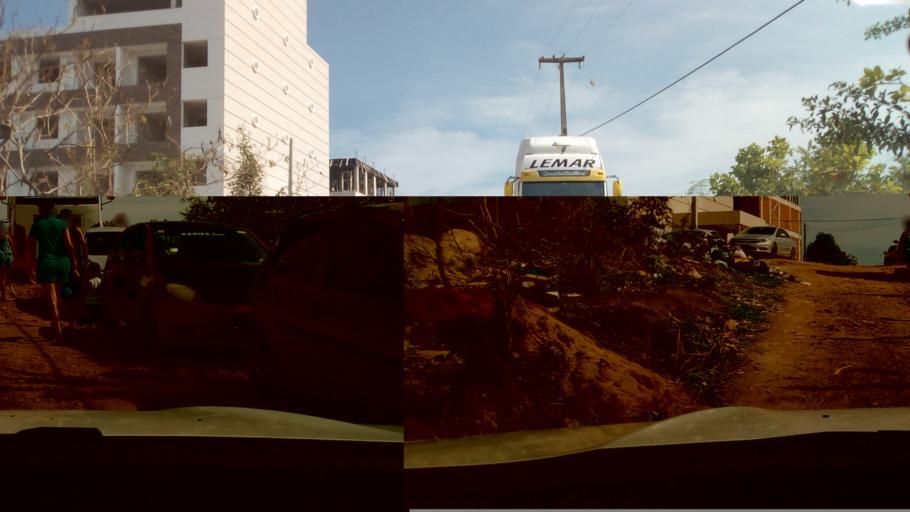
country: BR
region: Paraiba
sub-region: Conde
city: Conde
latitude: -7.2998
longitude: -34.8004
